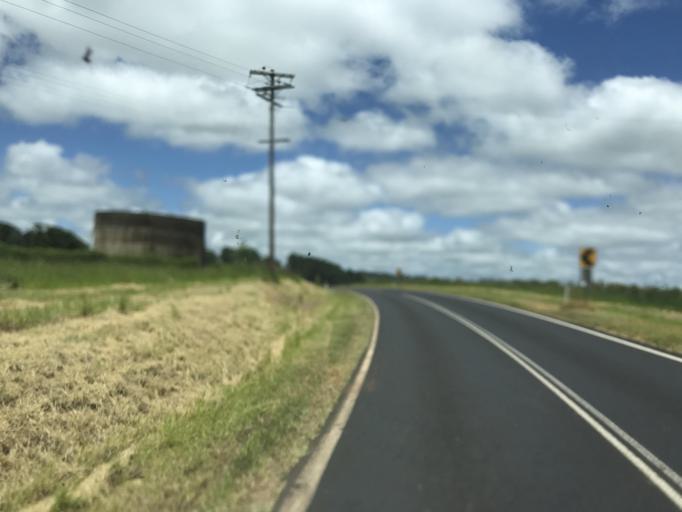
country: AU
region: Queensland
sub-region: Tablelands
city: Ravenshoe
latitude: -17.5091
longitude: 145.4737
